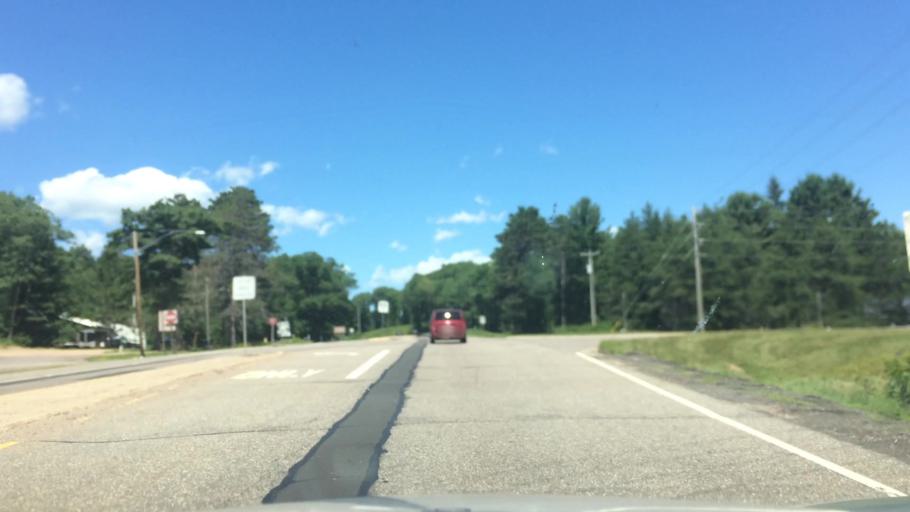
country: US
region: Wisconsin
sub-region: Vilas County
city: Lac du Flambeau
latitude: 45.7851
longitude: -89.7115
